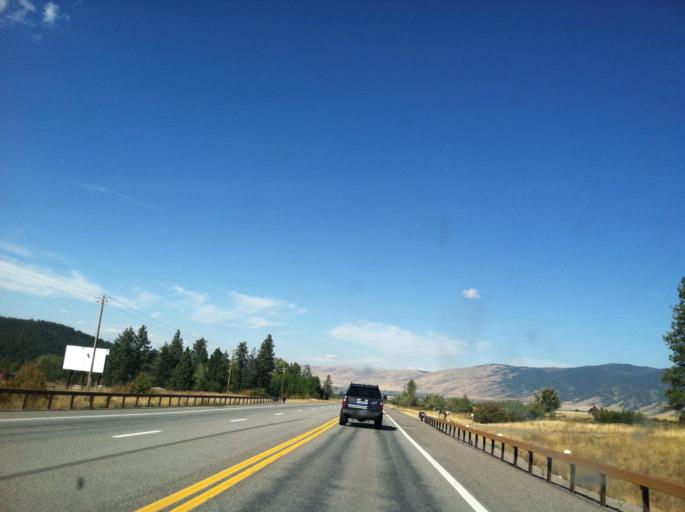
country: US
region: Montana
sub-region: Missoula County
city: Frenchtown
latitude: 47.0972
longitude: -114.0419
